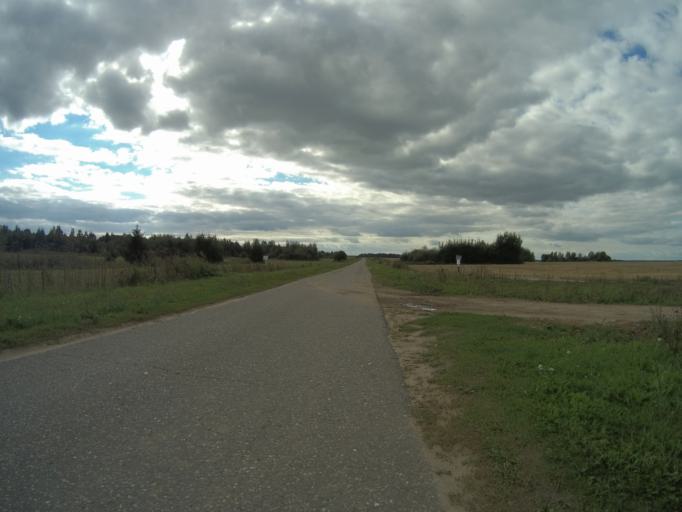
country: RU
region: Vladimir
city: Orgtrud
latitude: 56.3185
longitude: 40.6313
